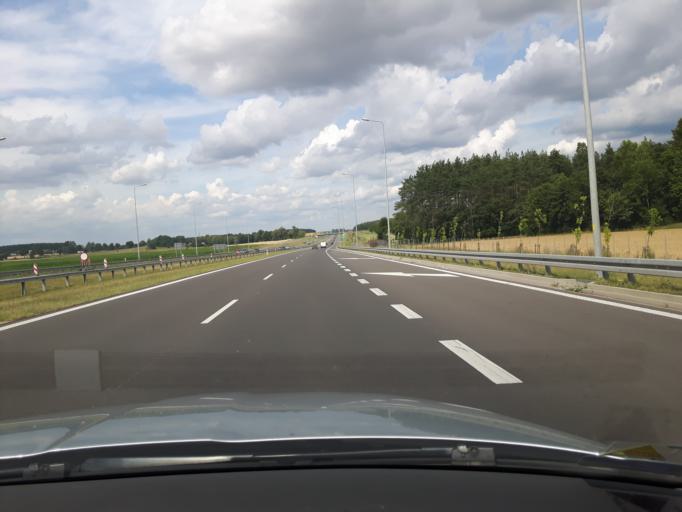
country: PL
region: Warmian-Masurian Voivodeship
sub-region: Powiat nidzicki
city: Nidzica
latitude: 53.3028
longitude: 20.4367
